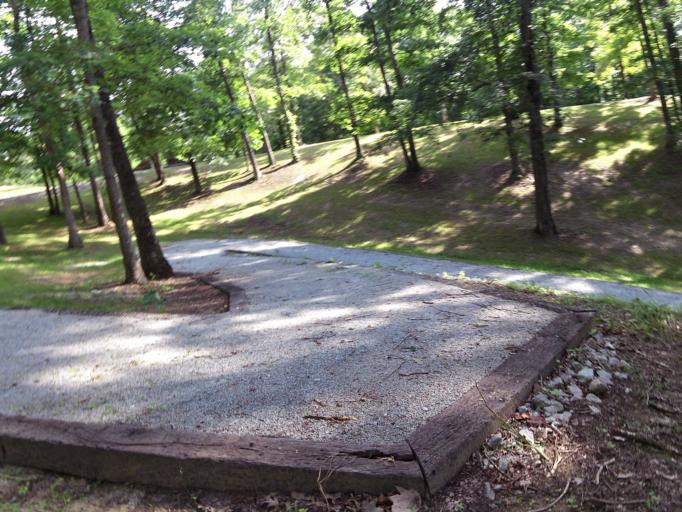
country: US
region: Tennessee
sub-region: Benton County
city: Camden
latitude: 36.0621
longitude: -88.1619
